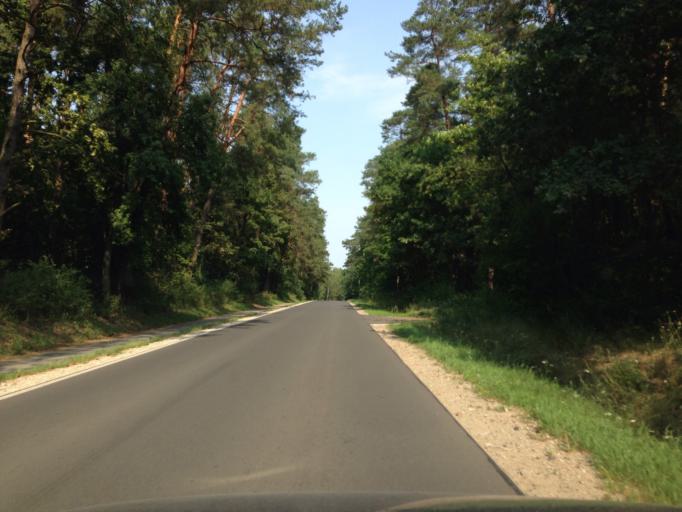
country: PL
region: Kujawsko-Pomorskie
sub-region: Powiat golubsko-dobrzynski
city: Golub-Dobrzyn
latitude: 53.0882
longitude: 19.0354
